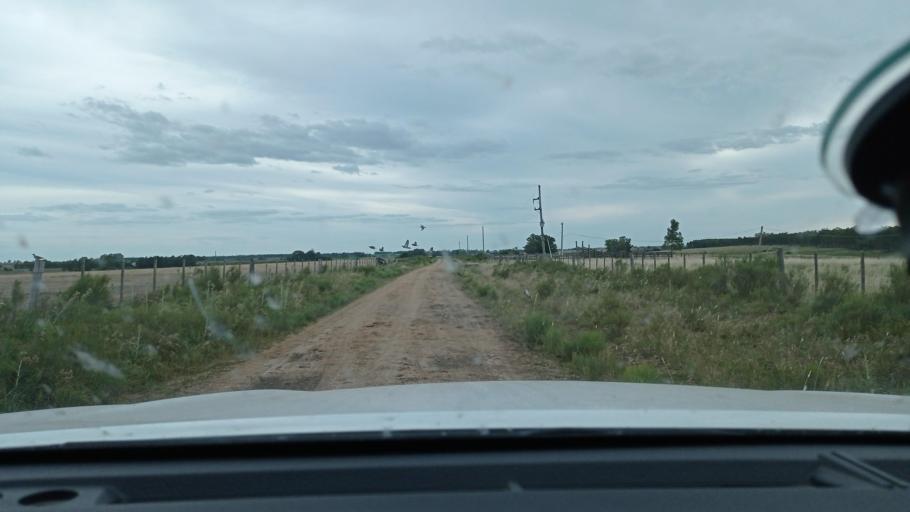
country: UY
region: Florida
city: Casupa
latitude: -34.1366
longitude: -55.8021
